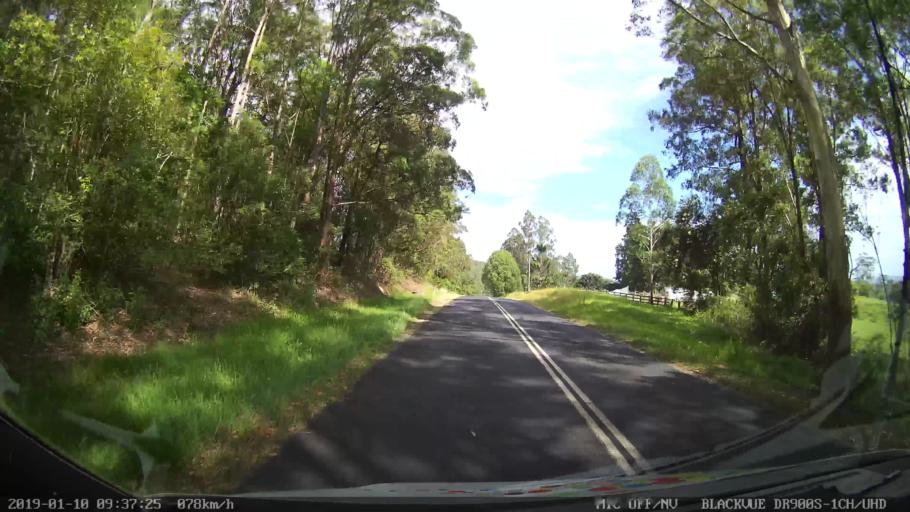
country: AU
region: New South Wales
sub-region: Coffs Harbour
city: Nana Glen
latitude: -30.1879
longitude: 153.0097
